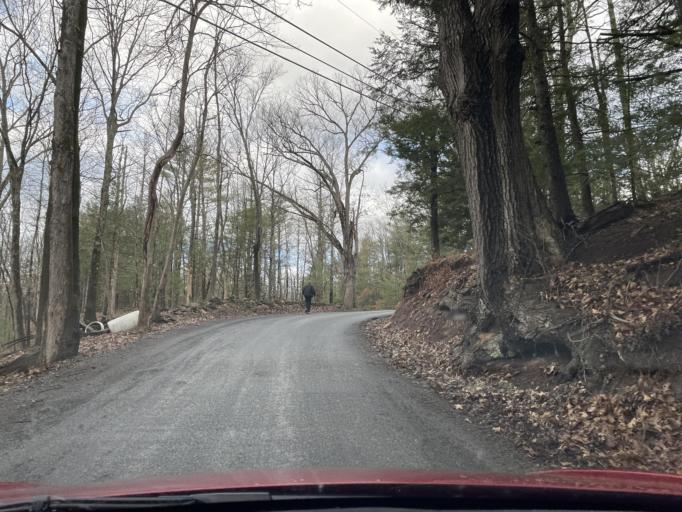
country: US
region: New York
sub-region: Ulster County
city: Manorville
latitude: 42.0818
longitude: -74.0423
